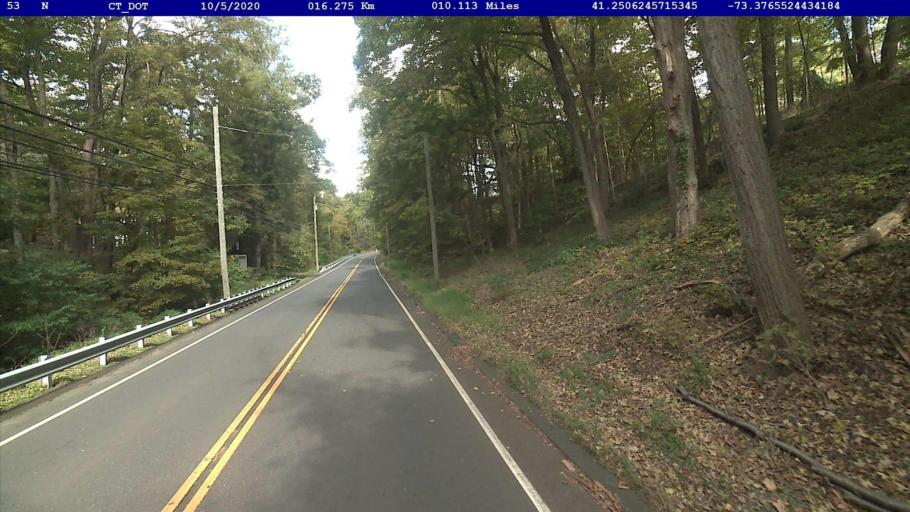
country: US
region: Connecticut
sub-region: Fairfield County
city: Georgetown
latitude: 41.2506
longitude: -73.3766
